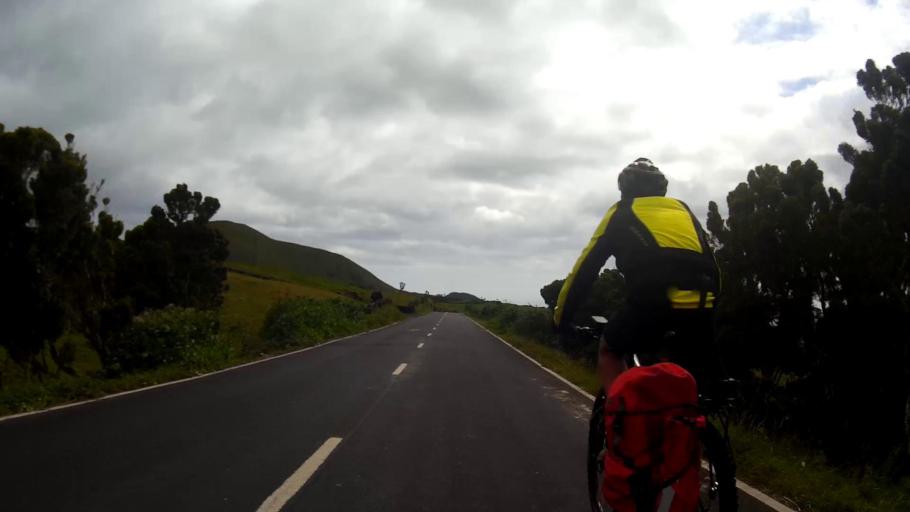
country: PT
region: Azores
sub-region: Madalena
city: Madalena
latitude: 38.4966
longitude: -28.4522
